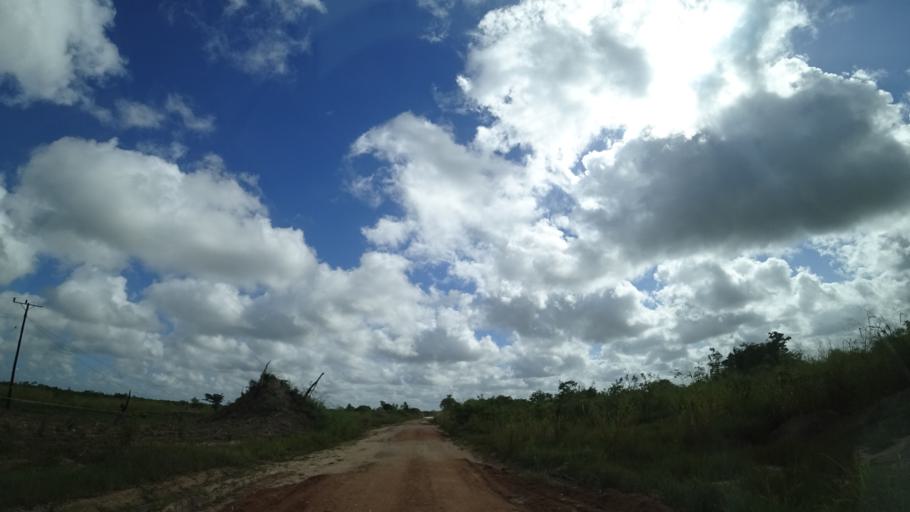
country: MZ
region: Sofala
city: Dondo
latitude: -19.4163
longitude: 34.7101
